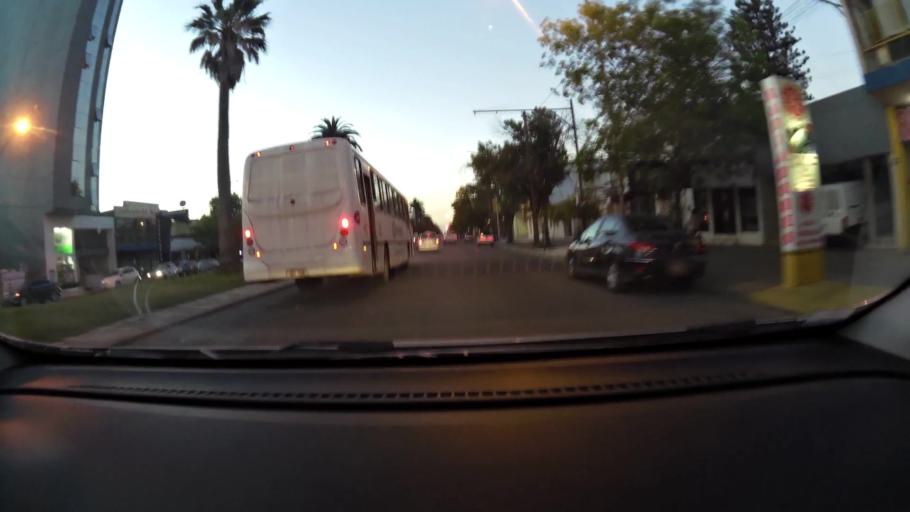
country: AR
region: Cordoba
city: Villa Maria
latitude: -32.4098
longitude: -63.2374
